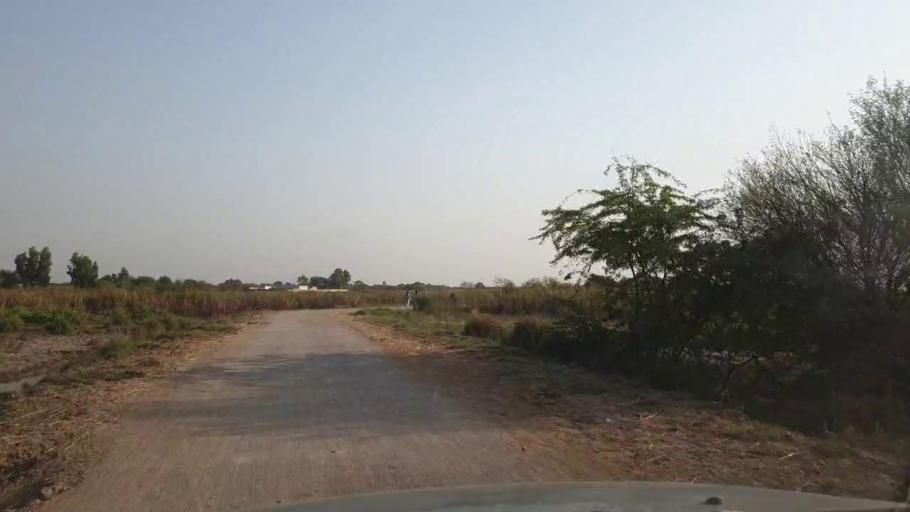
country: PK
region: Sindh
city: Bulri
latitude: 24.9476
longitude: 68.3426
